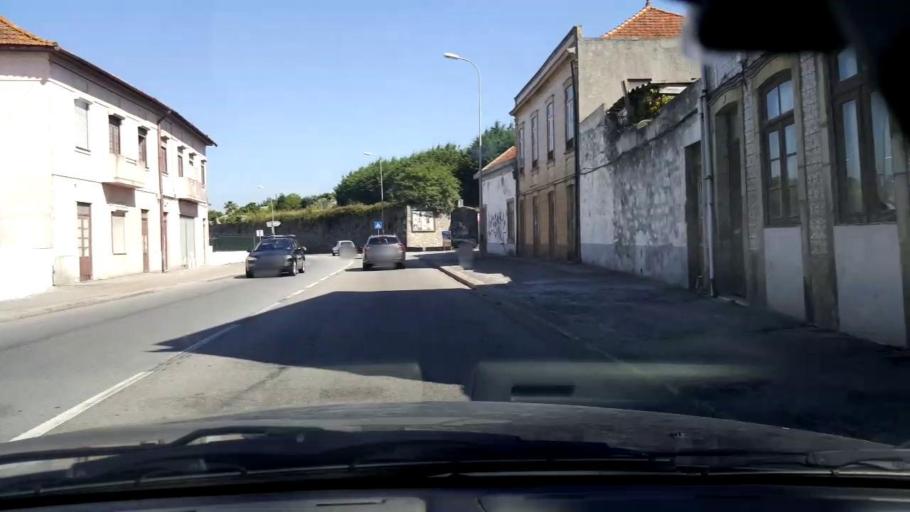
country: PT
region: Porto
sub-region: Vila do Conde
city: Vila do Conde
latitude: 41.3481
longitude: -8.7382
